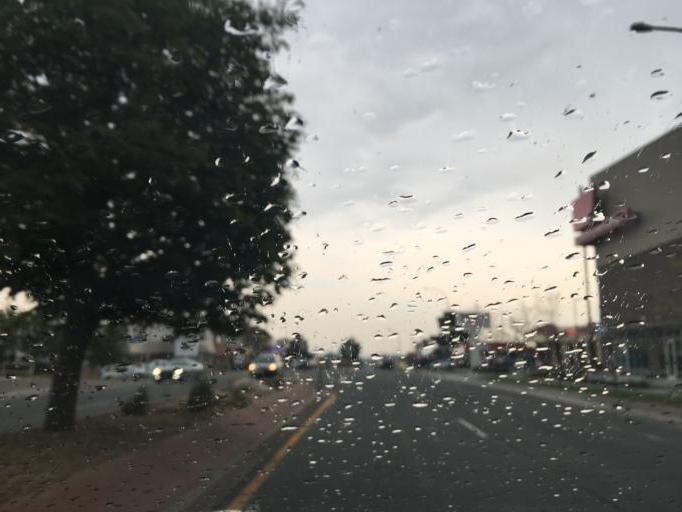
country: US
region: Colorado
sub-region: Jefferson County
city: Wheat Ridge
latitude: 39.7402
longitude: -105.1074
